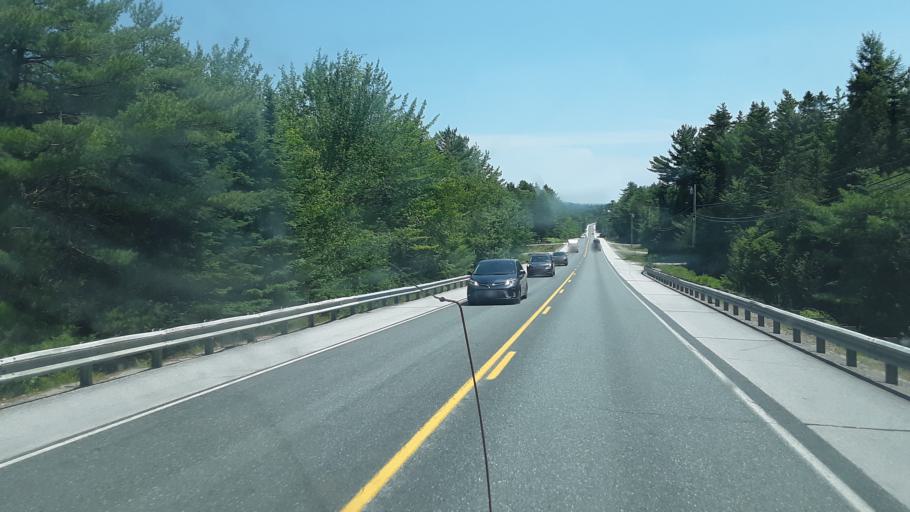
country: US
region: Maine
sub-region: Hancock County
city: Hancock
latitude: 44.5361
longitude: -68.2804
